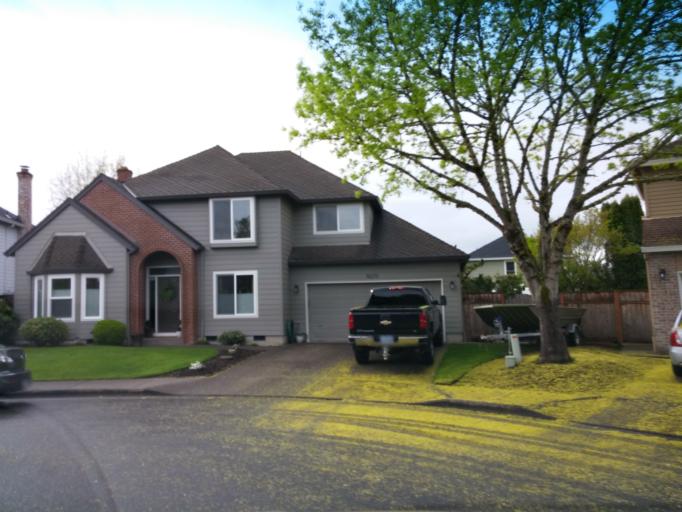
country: US
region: Oregon
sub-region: Washington County
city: Oak Hills
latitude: 45.5373
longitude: -122.8451
